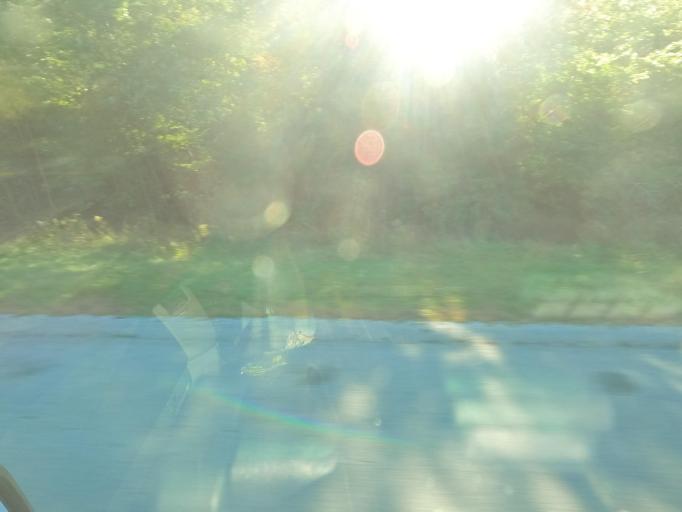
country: US
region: Tennessee
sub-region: Coffee County
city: New Union
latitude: 35.5418
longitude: -86.1789
